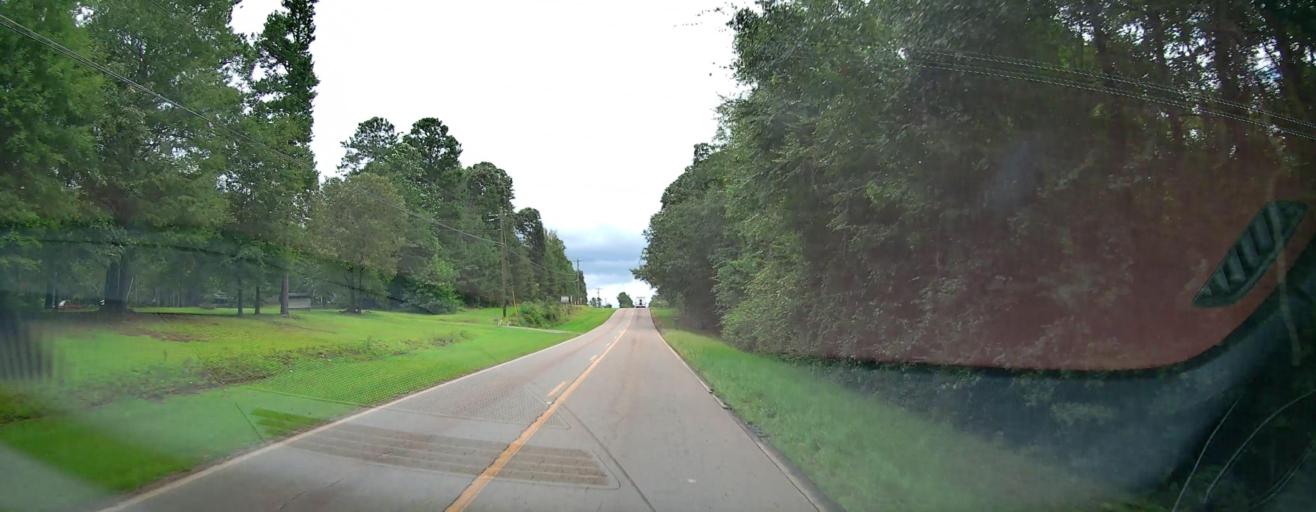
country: US
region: Georgia
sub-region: Bibb County
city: Macon
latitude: 32.7666
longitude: -83.4989
